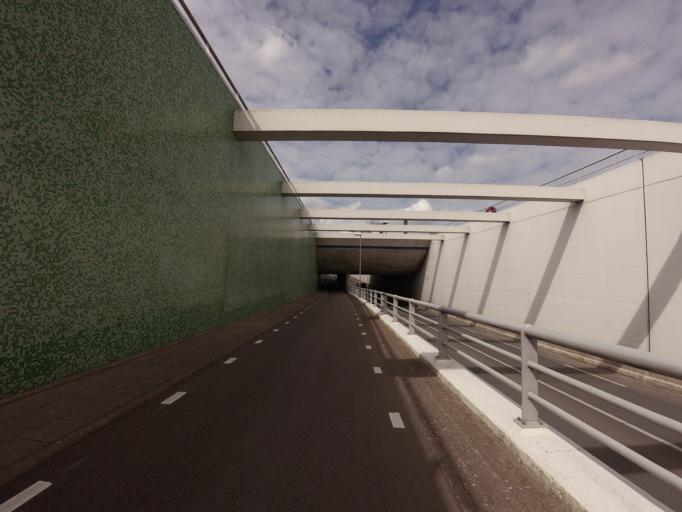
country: NL
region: Friesland
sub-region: Sudwest Fryslan
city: Woudsend
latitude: 52.9656
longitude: 5.6517
